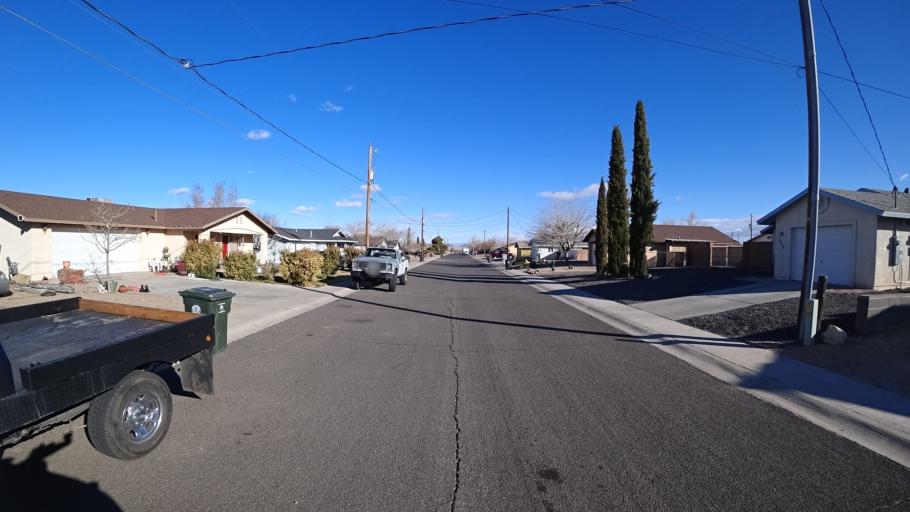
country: US
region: Arizona
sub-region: Mohave County
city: New Kingman-Butler
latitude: 35.2182
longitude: -113.9959
